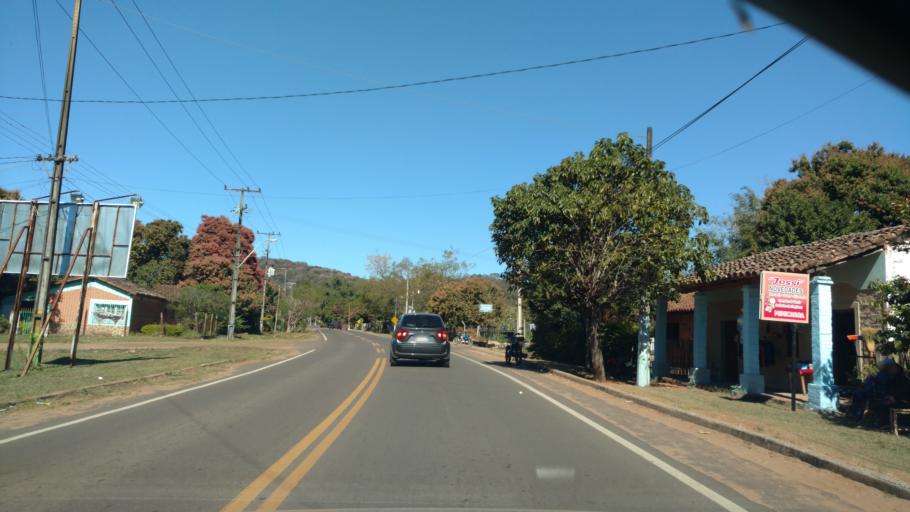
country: PY
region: Paraguari
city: Pirayu
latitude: -25.4894
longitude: -57.2392
